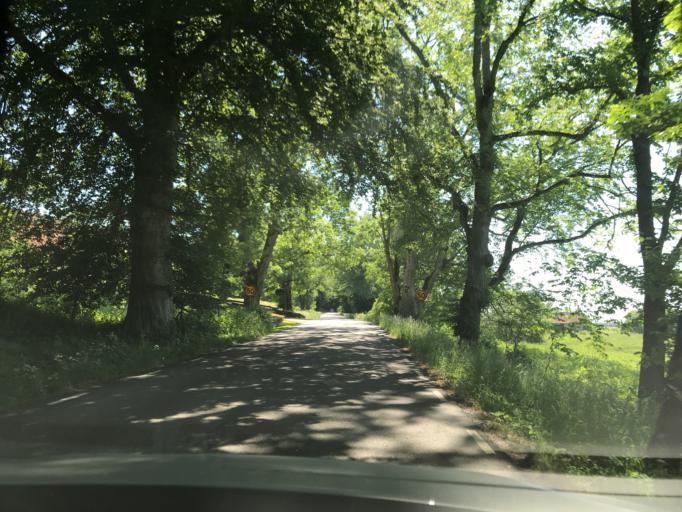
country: SE
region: Vaestra Goetaland
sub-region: Gotene Kommun
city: Kallby
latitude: 58.5812
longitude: 13.3728
